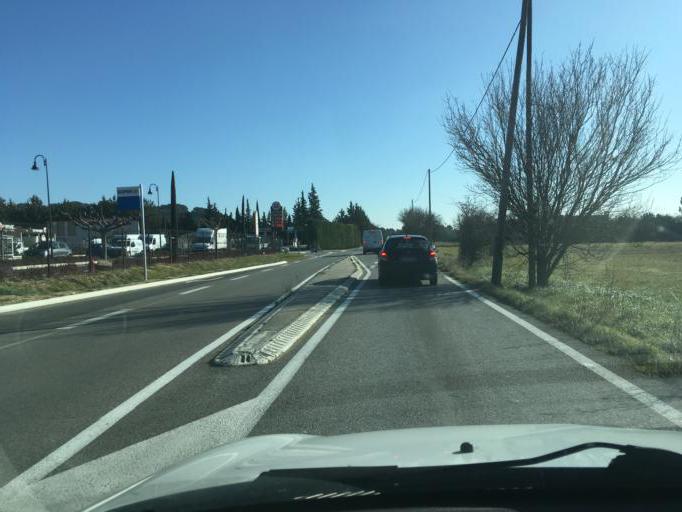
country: FR
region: Provence-Alpes-Cote d'Azur
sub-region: Departement du Vaucluse
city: Lauris
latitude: 43.7475
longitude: 5.3358
